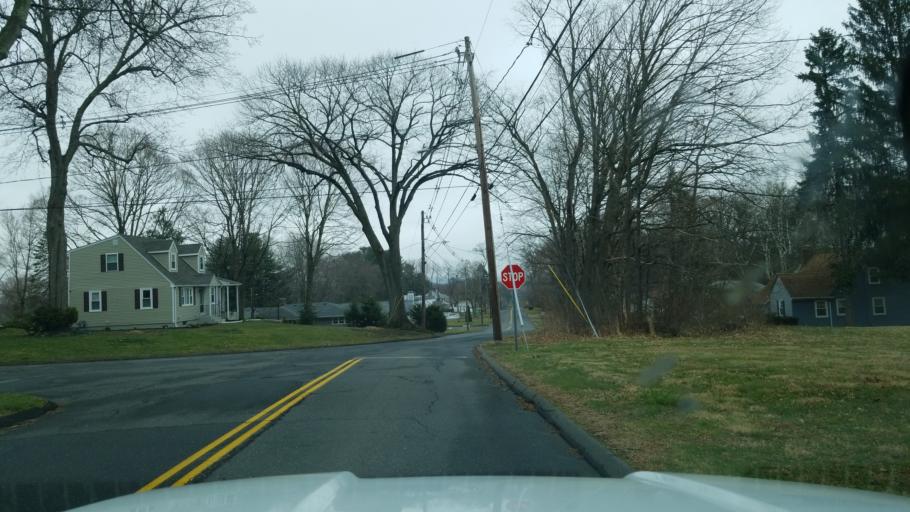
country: US
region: Connecticut
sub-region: Hartford County
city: Kensington
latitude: 41.6334
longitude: -72.7863
